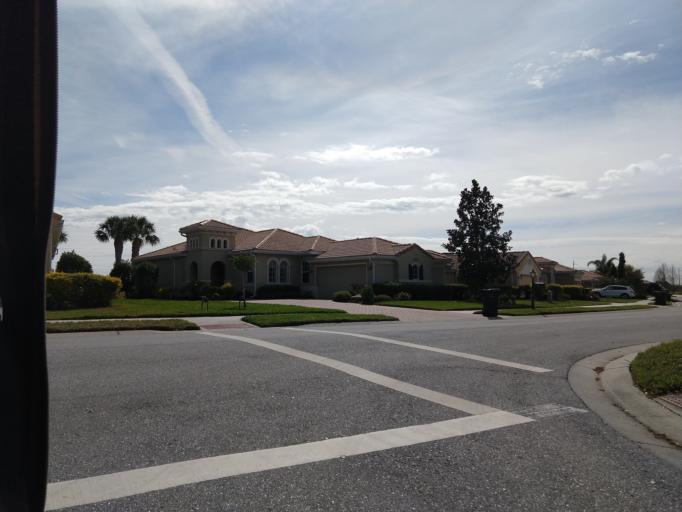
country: US
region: Florida
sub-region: Sarasota County
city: Nokomis
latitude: 27.1461
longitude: -82.3745
